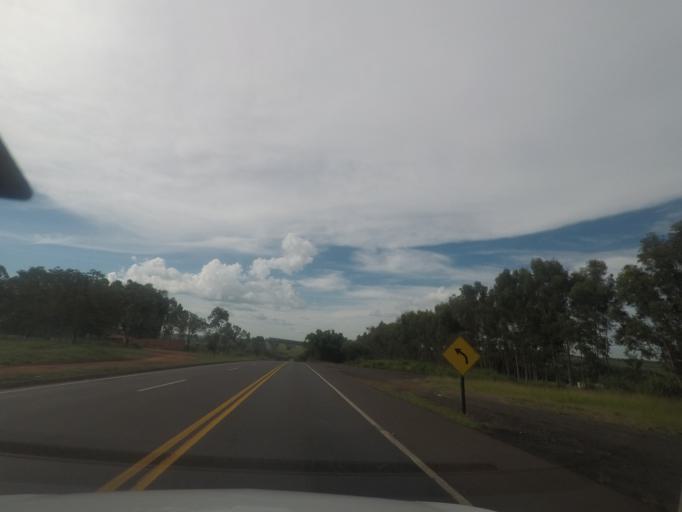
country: BR
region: Minas Gerais
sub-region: Prata
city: Prata
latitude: -19.2206
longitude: -48.9345
